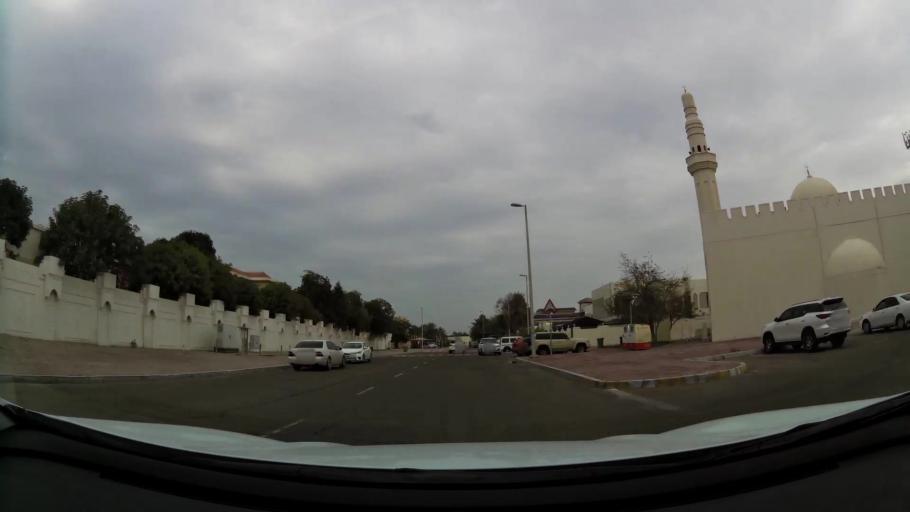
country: AE
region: Abu Dhabi
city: Abu Dhabi
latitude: 24.4335
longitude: 54.3836
